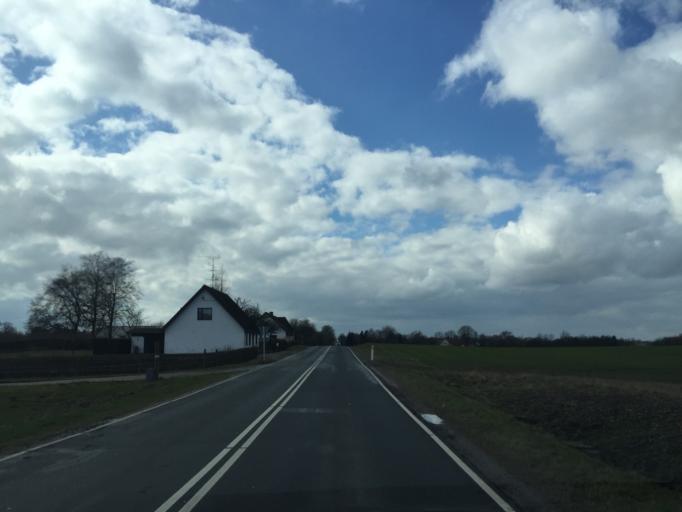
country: DK
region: South Denmark
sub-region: Svendborg Kommune
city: Svendborg
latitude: 55.1134
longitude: 10.5549
